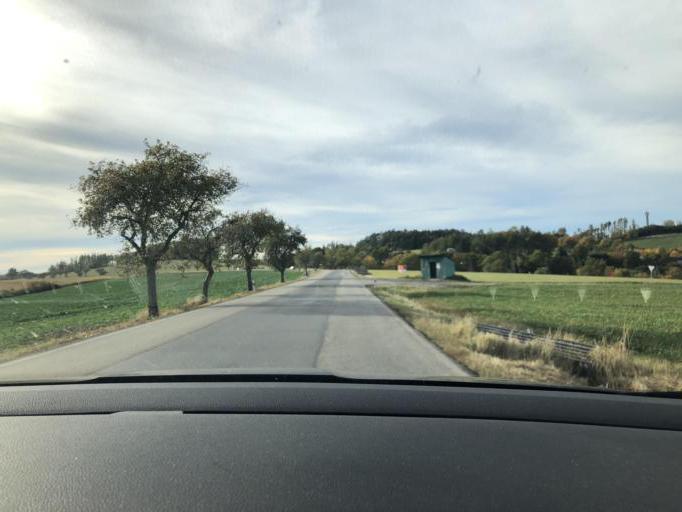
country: CZ
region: Central Bohemia
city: Divisov
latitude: 49.7871
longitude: 14.8386
